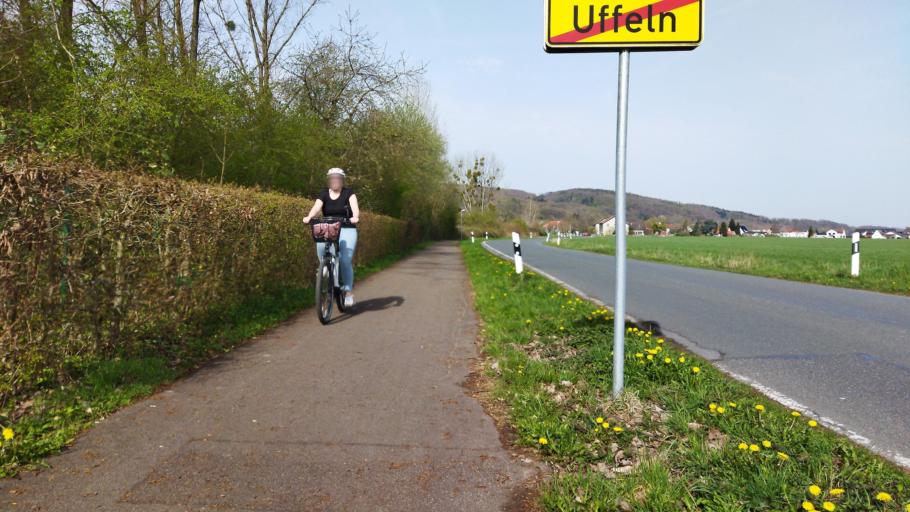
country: DE
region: North Rhine-Westphalia
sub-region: Regierungsbezirk Detmold
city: Vlotho
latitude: 52.1686
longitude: 8.8784
